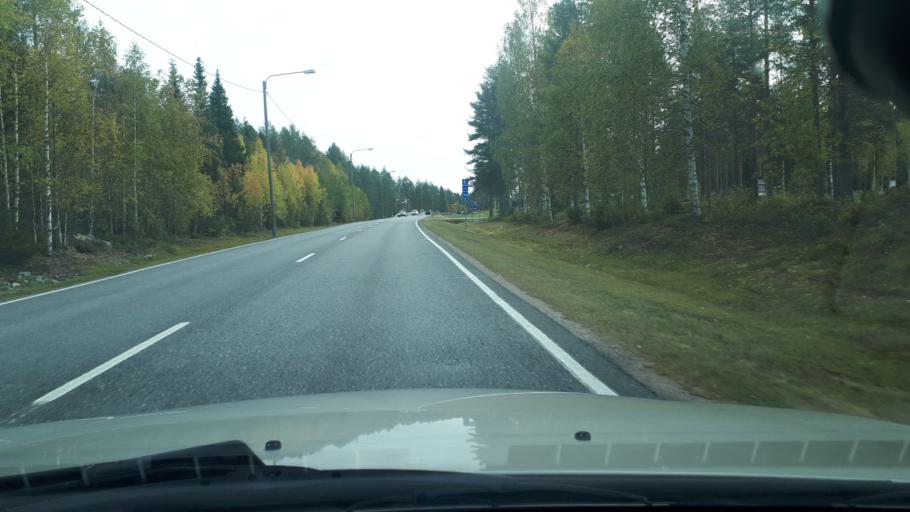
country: FI
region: Lapland
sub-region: Rovaniemi
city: Ranua
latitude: 65.9454
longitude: 26.4612
